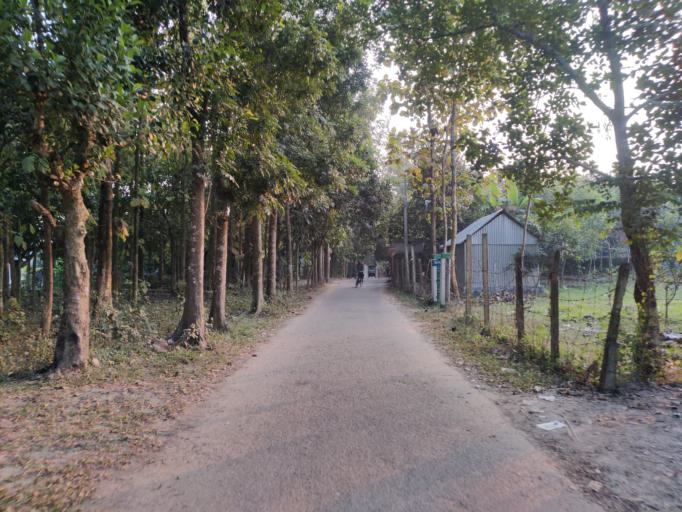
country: BD
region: Dhaka
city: Bajitpur
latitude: 24.1568
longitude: 90.7639
